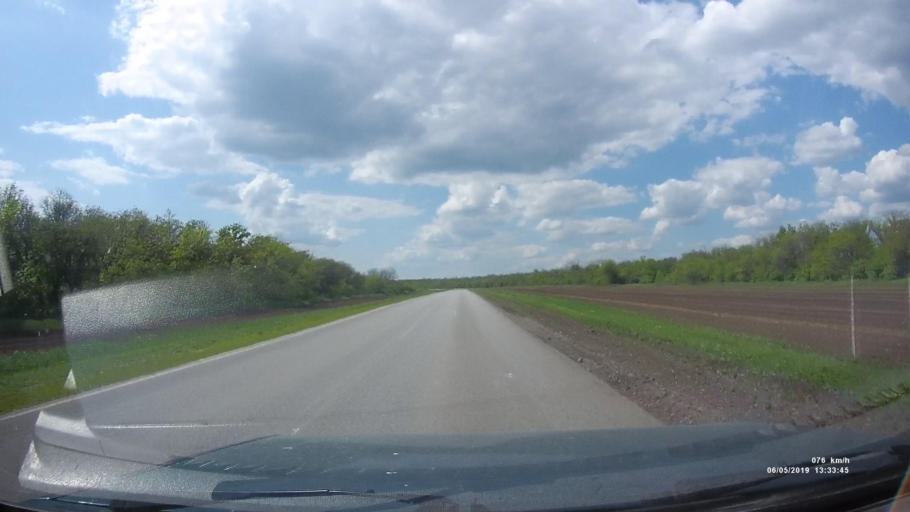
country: RU
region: Rostov
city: Ust'-Donetskiy
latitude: 47.6917
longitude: 40.7745
